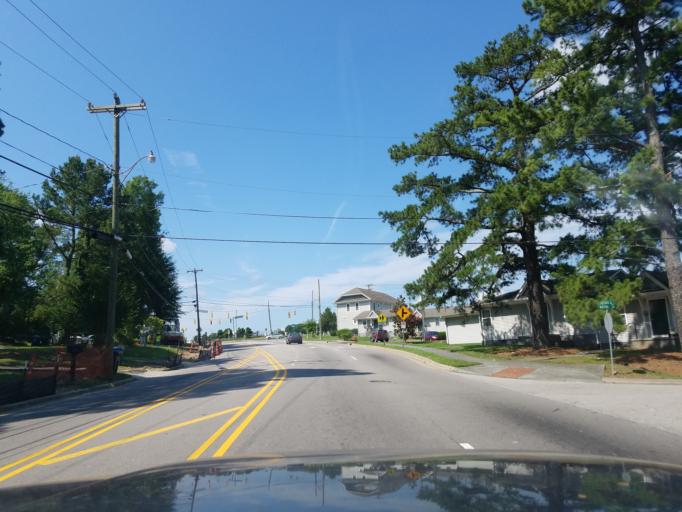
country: US
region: North Carolina
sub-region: Durham County
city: Durham
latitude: 35.9610
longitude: -78.9099
